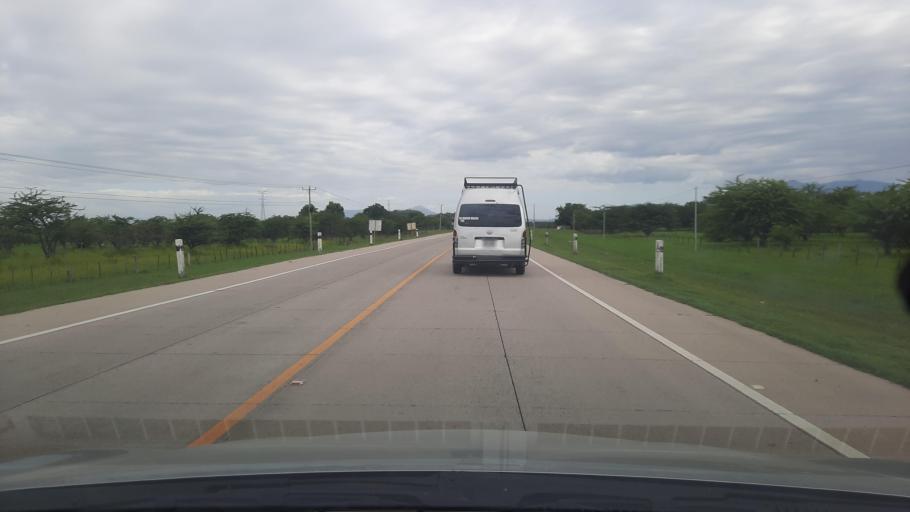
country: NI
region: Chinandega
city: Somotillo
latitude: 12.8861
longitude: -86.8501
